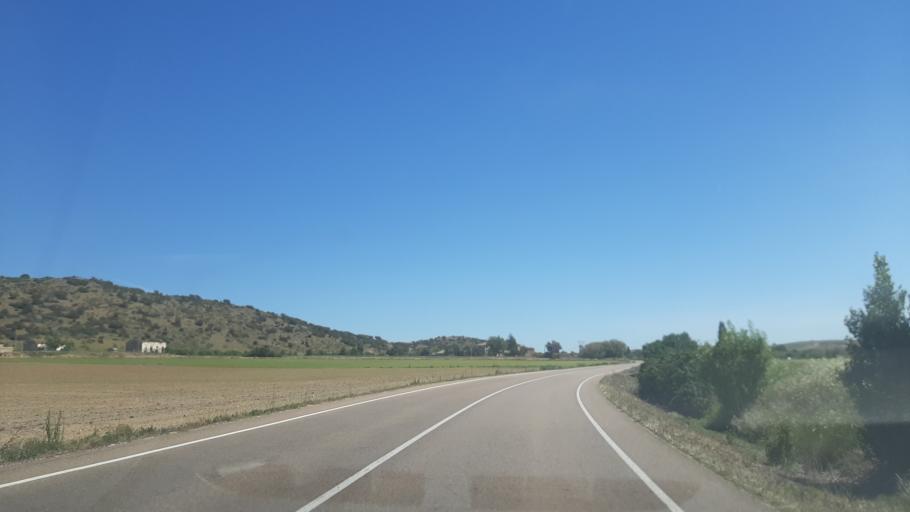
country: ES
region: Castille and Leon
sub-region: Provincia de Salamanca
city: Alba de Tormes
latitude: 40.8044
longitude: -5.5372
